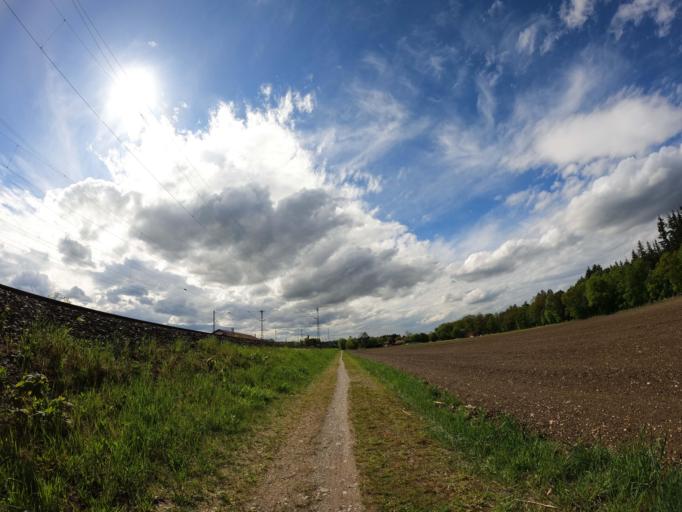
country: DE
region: Bavaria
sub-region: Upper Bavaria
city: Kirchseeon
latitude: 48.0832
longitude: 11.8620
